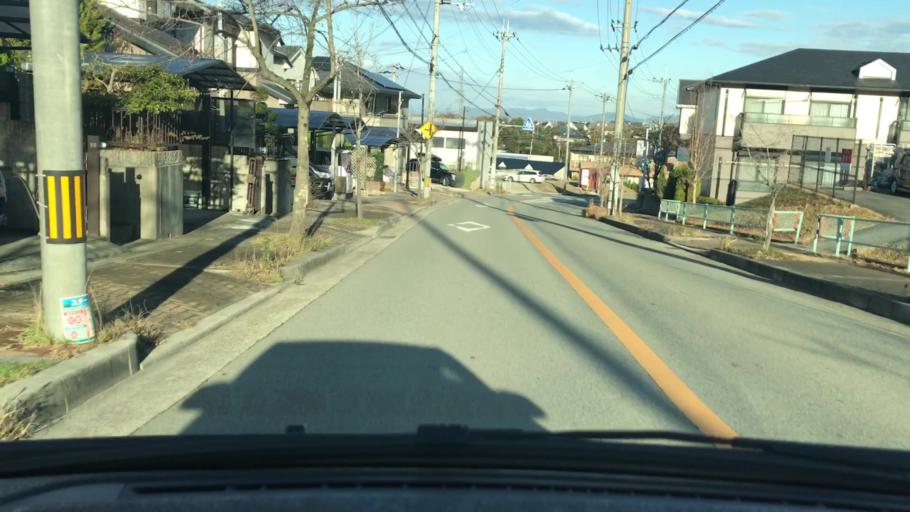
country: JP
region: Hyogo
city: Sandacho
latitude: 34.8263
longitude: 135.2506
